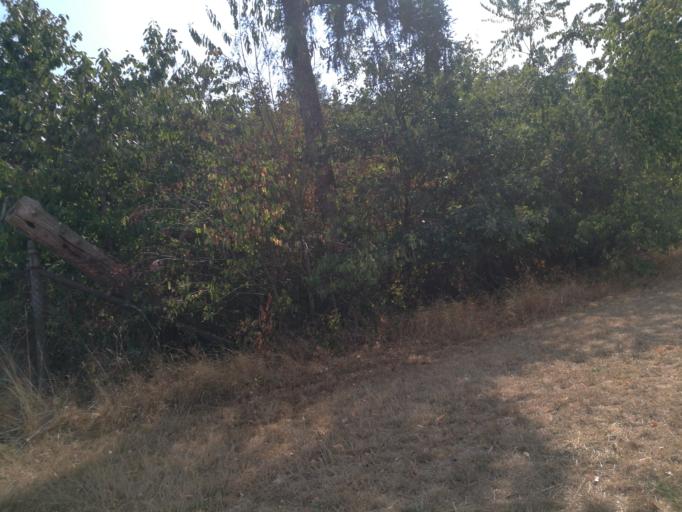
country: DE
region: Bavaria
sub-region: Regierungsbezirk Mittelfranken
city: Veitsbronn
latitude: 49.4972
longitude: 10.8975
